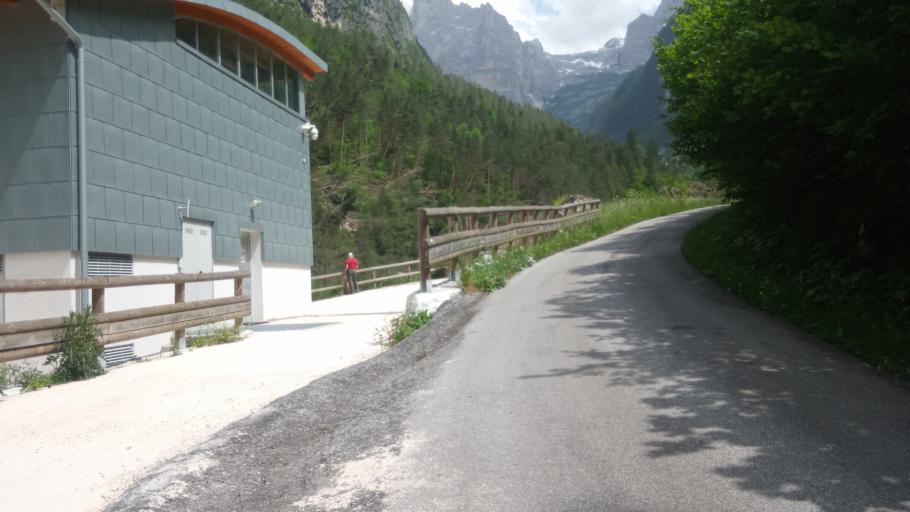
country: IT
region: Veneto
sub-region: Provincia di Belluno
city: Taibon Agordino
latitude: 46.3239
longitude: 12.0139
